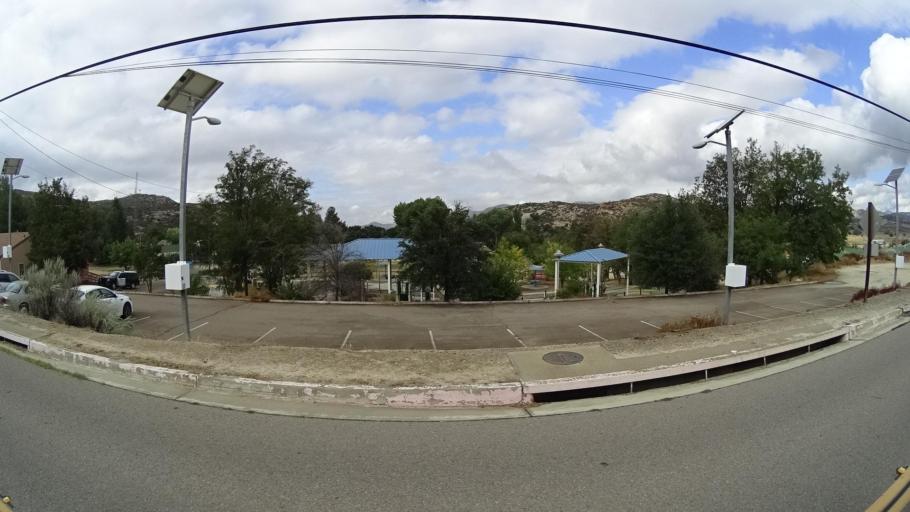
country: US
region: California
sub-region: San Diego County
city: Campo
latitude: 32.6089
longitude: -116.4696
